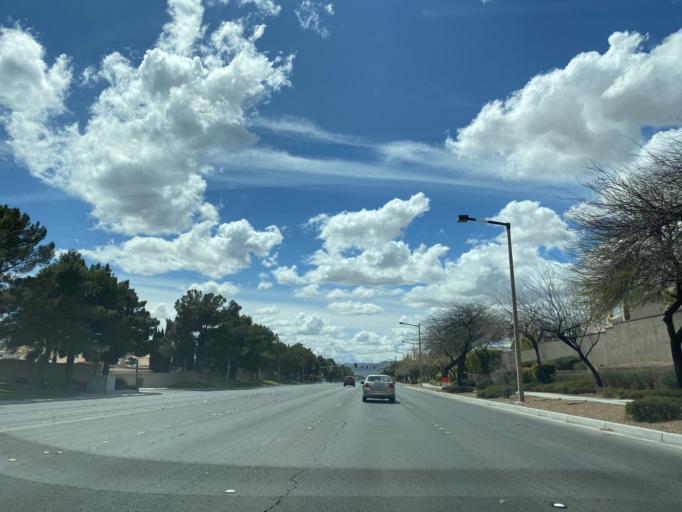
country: US
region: Nevada
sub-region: Clark County
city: Summerlin South
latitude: 36.1394
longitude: -115.3154
